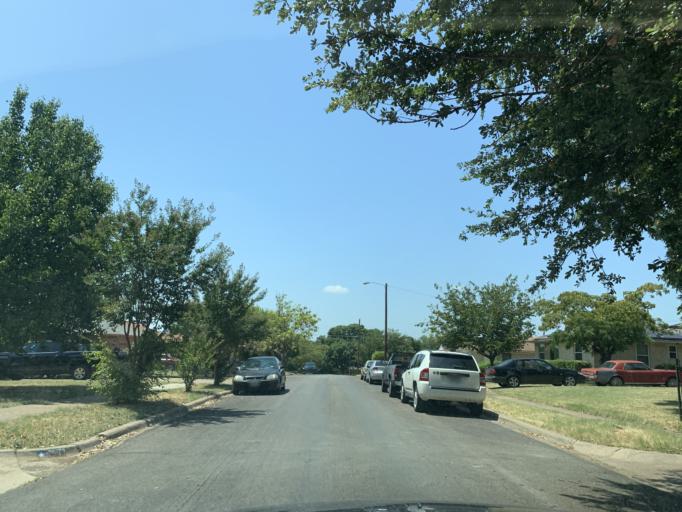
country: US
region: Texas
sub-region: Dallas County
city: Dallas
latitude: 32.6932
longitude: -96.8077
